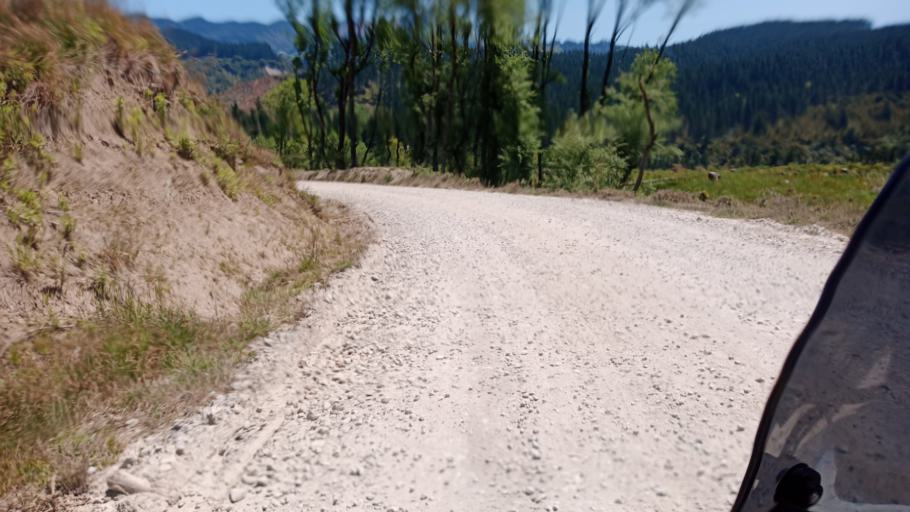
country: NZ
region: Gisborne
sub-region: Gisborne District
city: Gisborne
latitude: -38.2857
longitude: 178.0100
